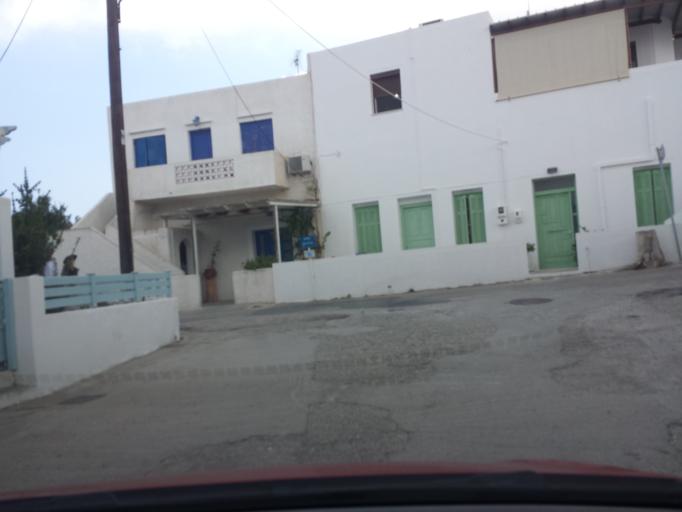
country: GR
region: South Aegean
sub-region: Nomos Kykladon
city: Milos
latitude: 36.7407
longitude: 24.4250
